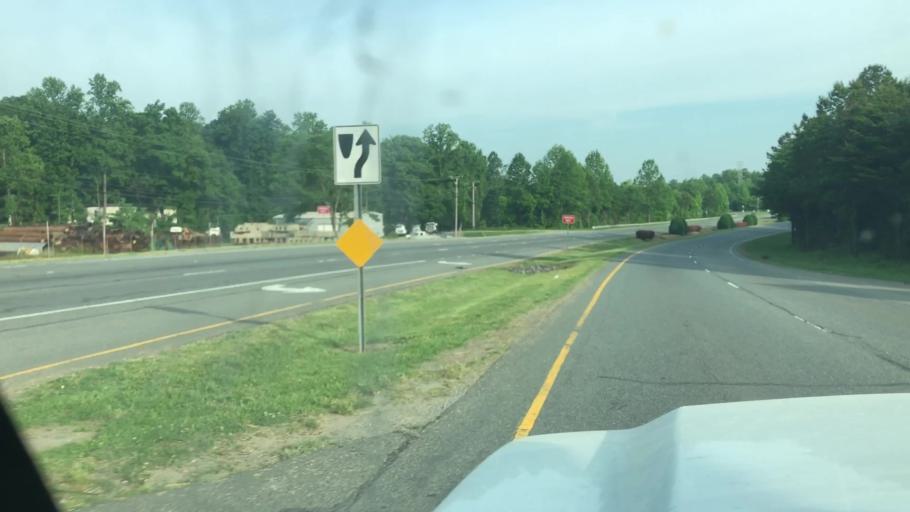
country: US
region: North Carolina
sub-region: Gaston County
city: Mount Holly
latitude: 35.2944
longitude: -80.9175
